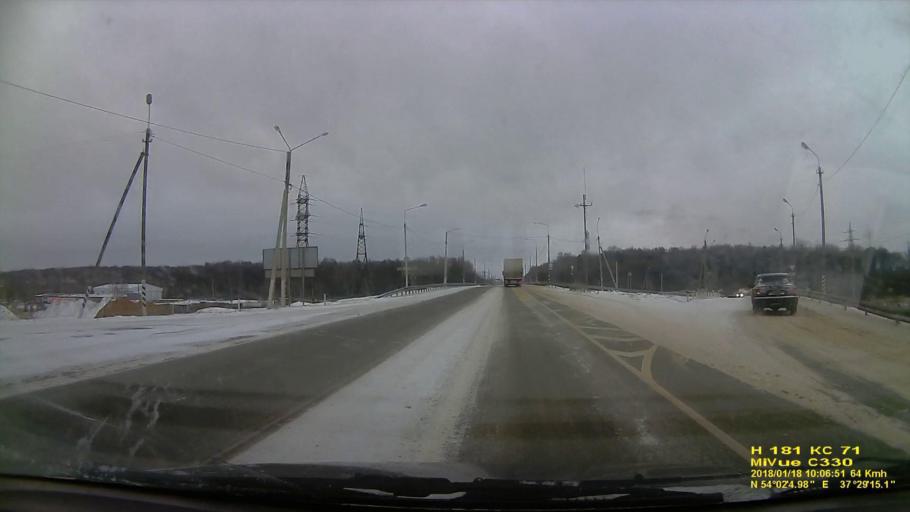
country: RU
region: Tula
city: Pervomayskiy
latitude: 54.0342
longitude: 37.4878
